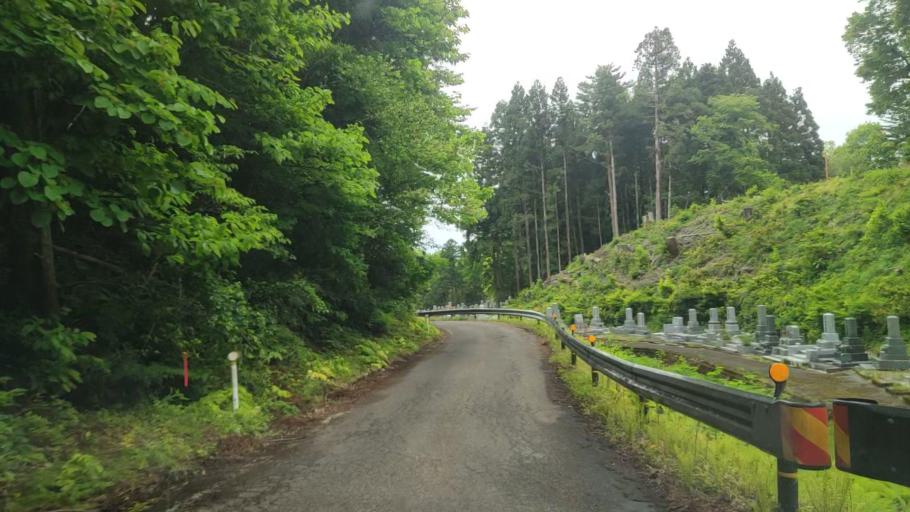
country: JP
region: Niigata
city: Kamo
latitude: 37.7158
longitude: 139.0864
